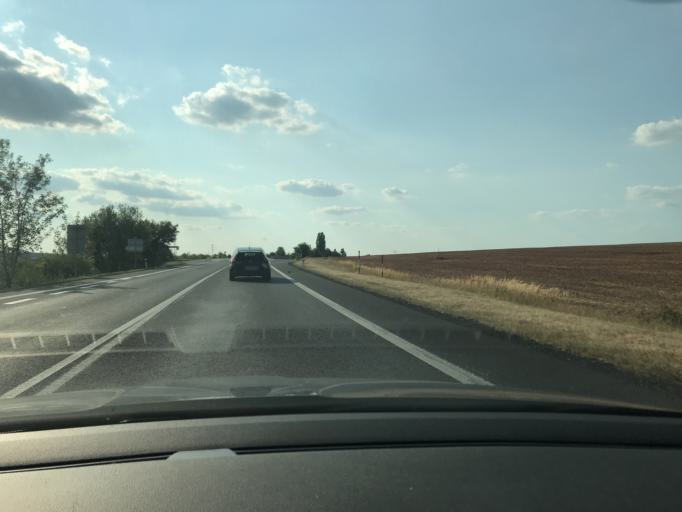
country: CZ
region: Central Bohemia
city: Klobuky
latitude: 50.2773
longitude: 13.9681
